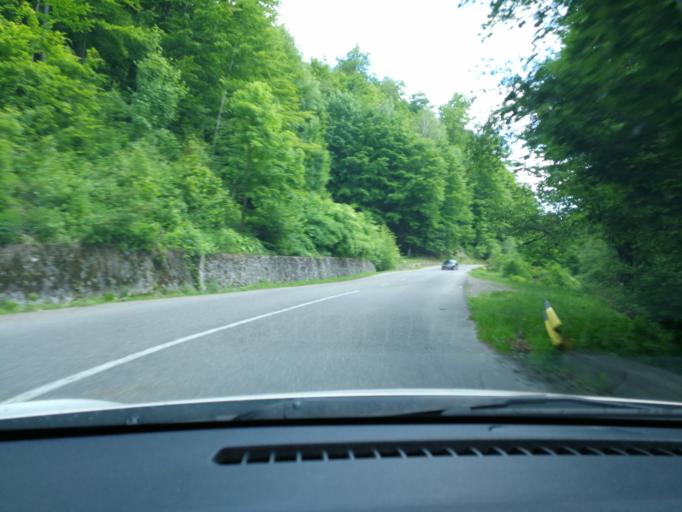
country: RO
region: Prahova
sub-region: Comuna Valea Doftanei
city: Tesila
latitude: 45.2688
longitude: 25.7334
